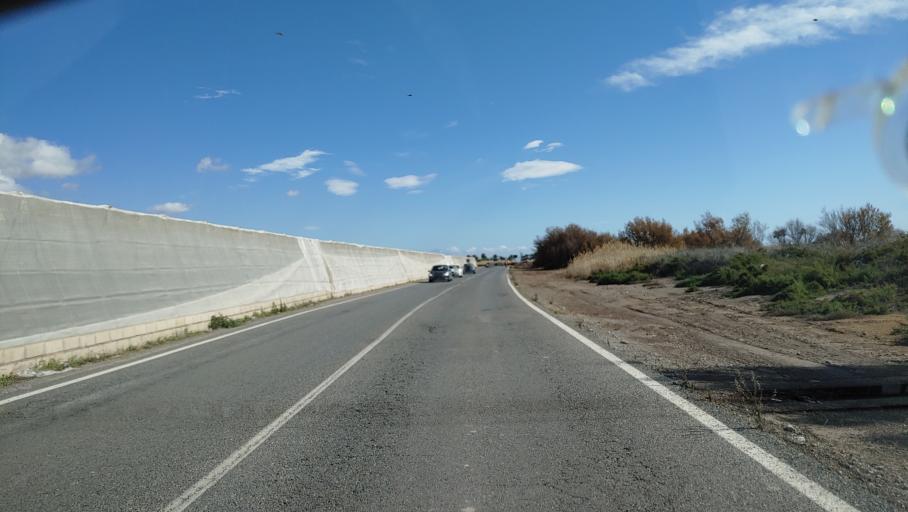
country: ES
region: Andalusia
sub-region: Provincia de Almeria
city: Roquetas de Mar
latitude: 36.7902
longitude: -2.5952
